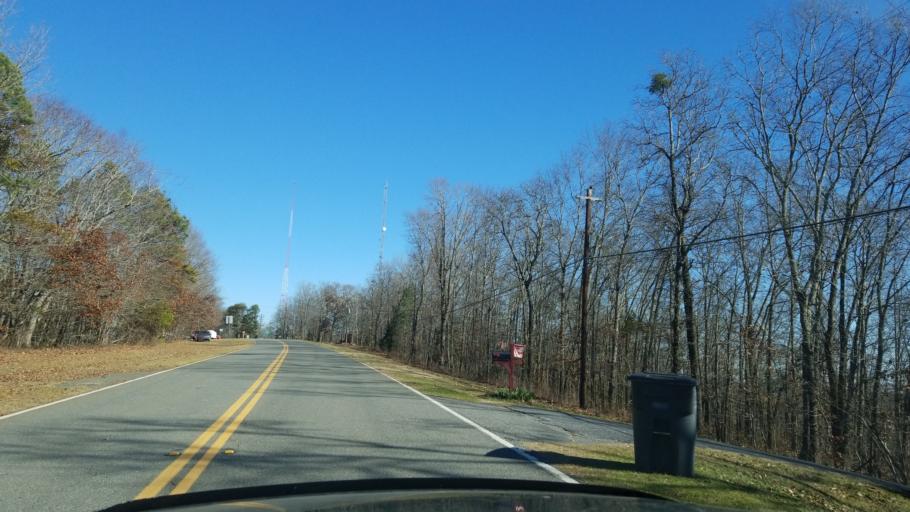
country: US
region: Georgia
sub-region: Meriwether County
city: Manchester
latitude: 32.8437
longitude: -84.6273
